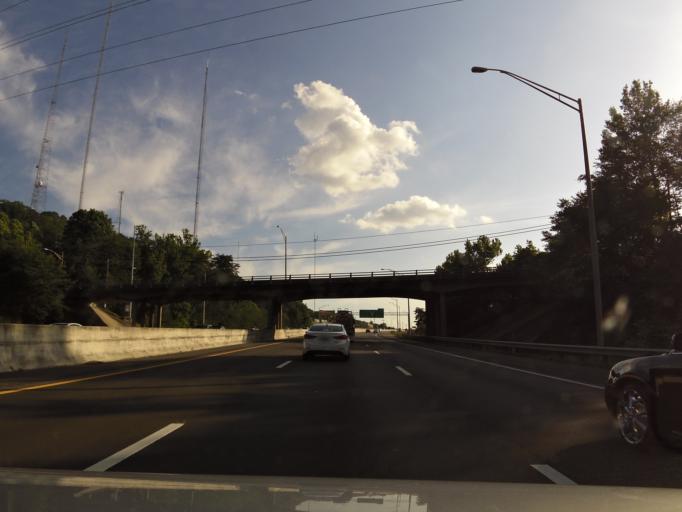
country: US
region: Tennessee
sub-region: Knox County
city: Knoxville
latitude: 36.0102
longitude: -83.9377
